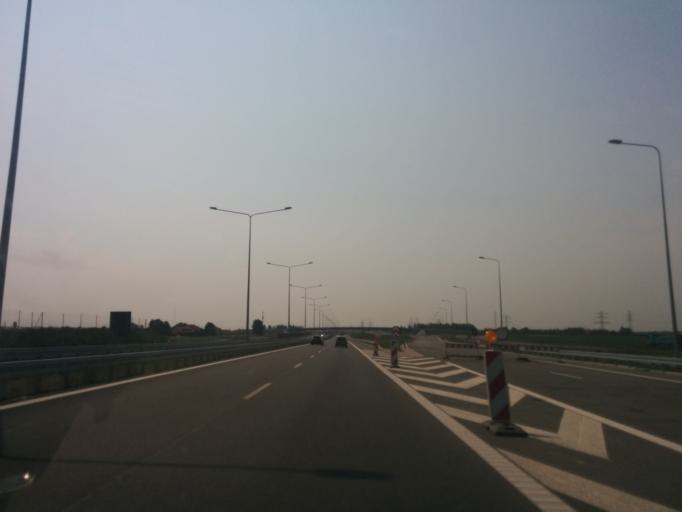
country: PL
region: Masovian Voivodeship
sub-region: Powiat pruszkowski
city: Nowe Grocholice
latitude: 52.1356
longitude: 20.8804
